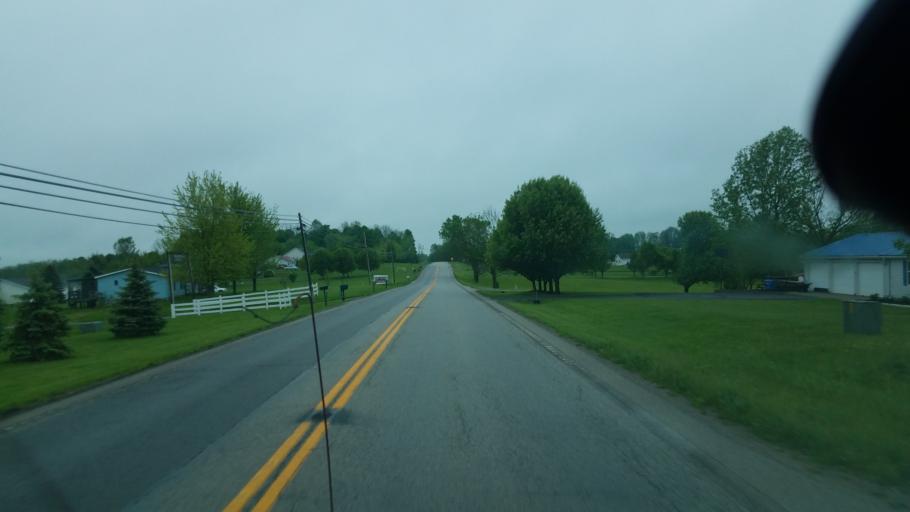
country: US
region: Ohio
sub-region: Highland County
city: Hillsboro
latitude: 39.2729
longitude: -83.5954
